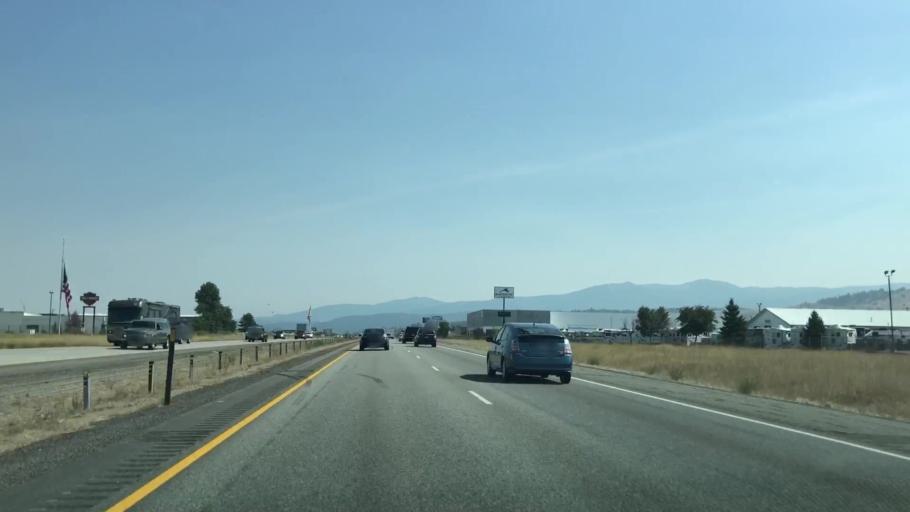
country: US
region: Washington
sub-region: Spokane County
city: Liberty Lake
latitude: 47.6648
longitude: -117.1517
